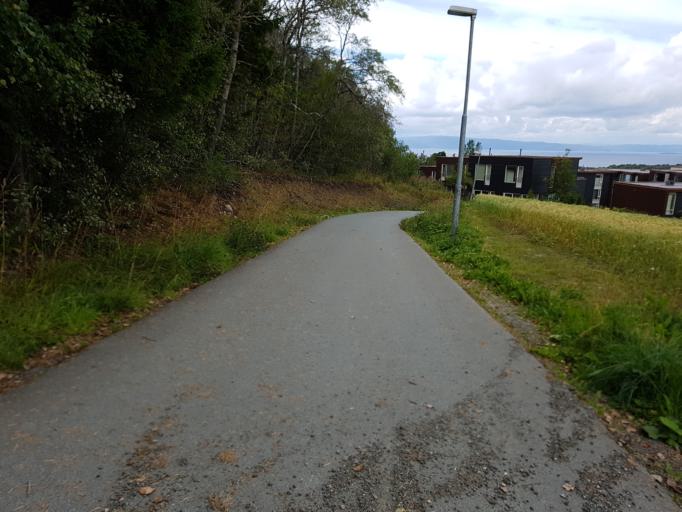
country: NO
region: Sor-Trondelag
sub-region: Trondheim
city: Trondheim
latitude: 63.4167
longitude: 10.4740
